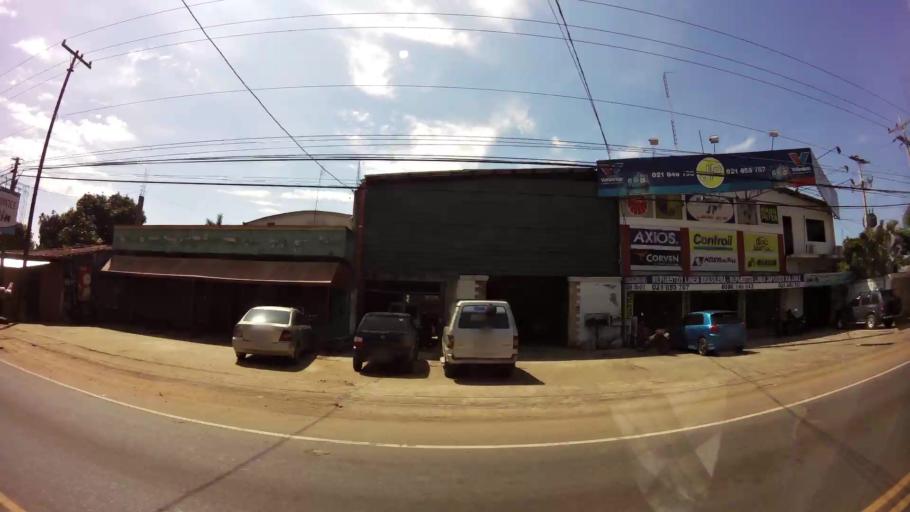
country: PY
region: Central
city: San Lorenzo
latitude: -25.2780
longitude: -57.4975
